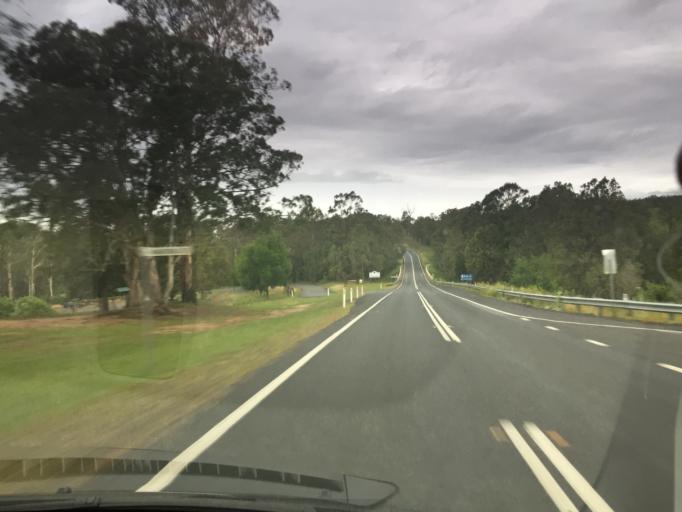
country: AU
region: New South Wales
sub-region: Bega Valley
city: Bega
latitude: -36.6339
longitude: 149.5771
